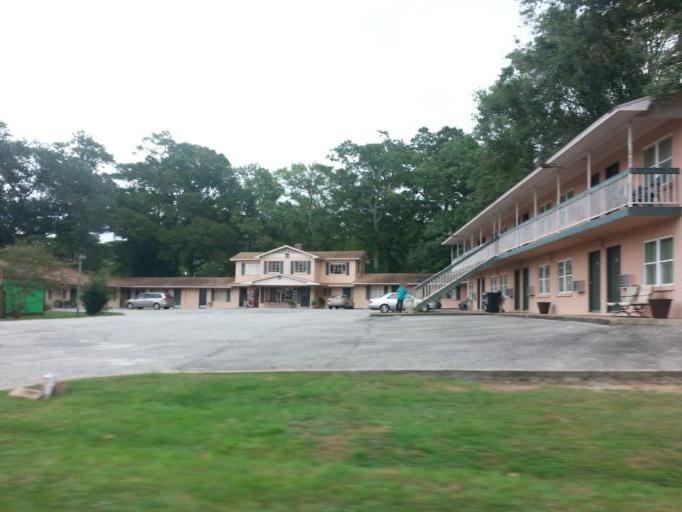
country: US
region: Alabama
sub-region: Baldwin County
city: Fairhope
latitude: 30.5129
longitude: -87.9183
